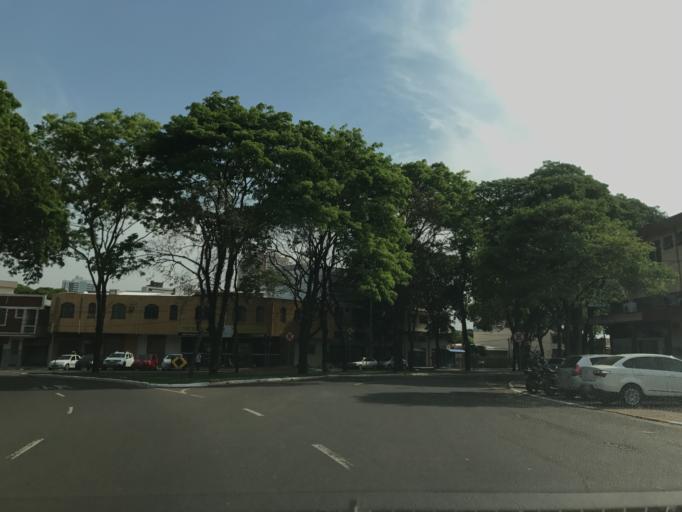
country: BR
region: Parana
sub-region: Maringa
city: Maringa
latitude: -23.4270
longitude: -51.9222
